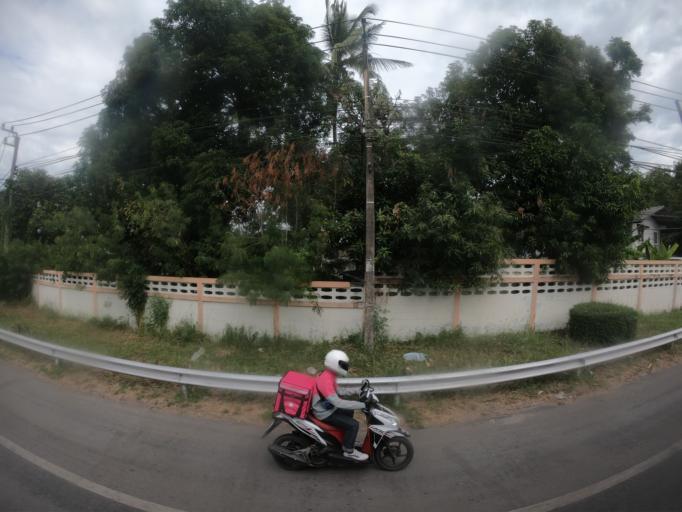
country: TH
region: Maha Sarakham
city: Maha Sarakham
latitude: 16.2035
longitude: 103.2879
